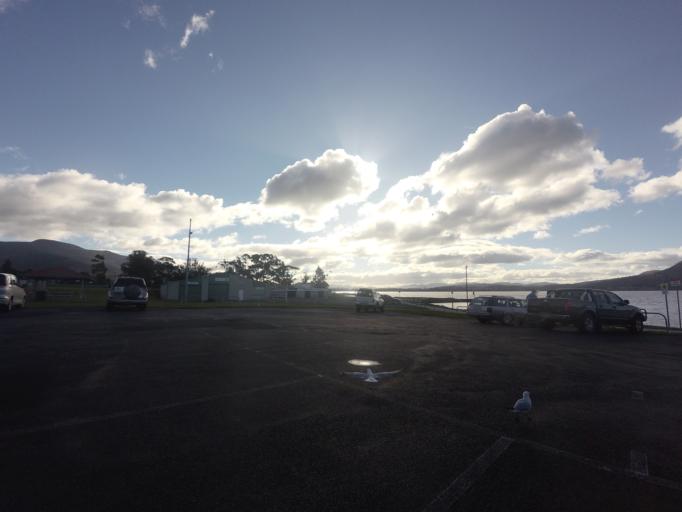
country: AU
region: Tasmania
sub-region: Glenorchy
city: Glenorchy
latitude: -42.8223
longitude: 147.2695
